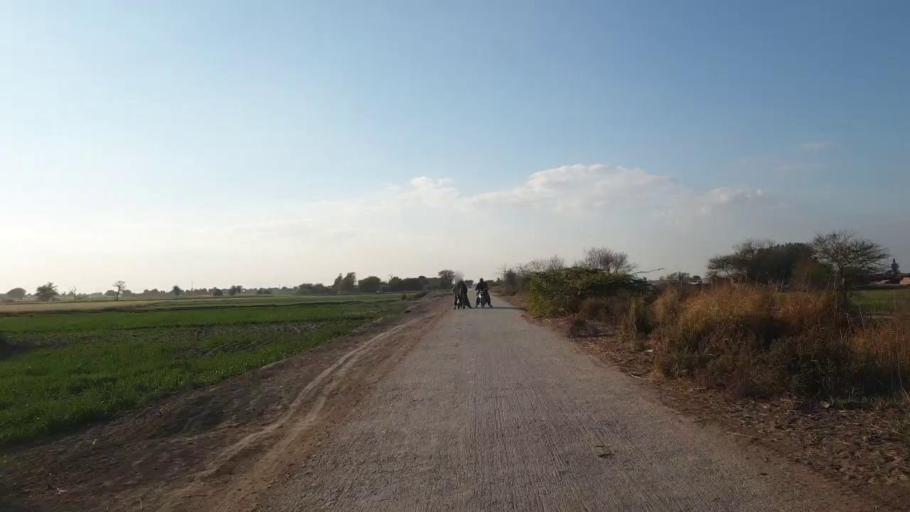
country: PK
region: Sindh
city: Shahpur Chakar
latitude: 26.1431
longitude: 68.5429
